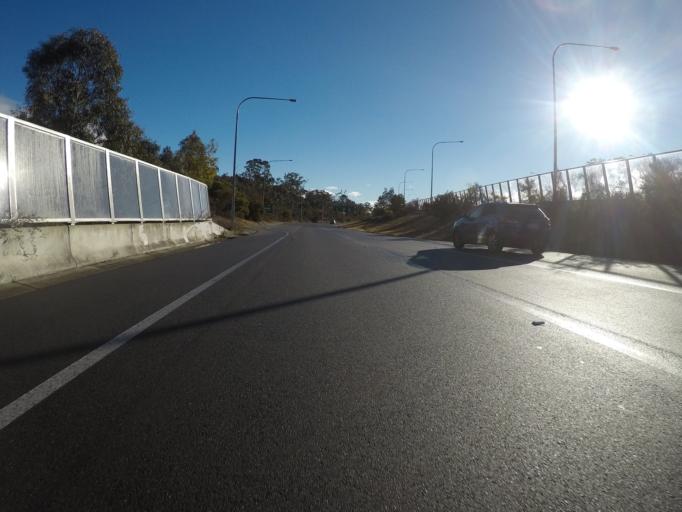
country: AU
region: Australian Capital Territory
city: Macquarie
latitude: -35.2597
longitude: 149.0872
